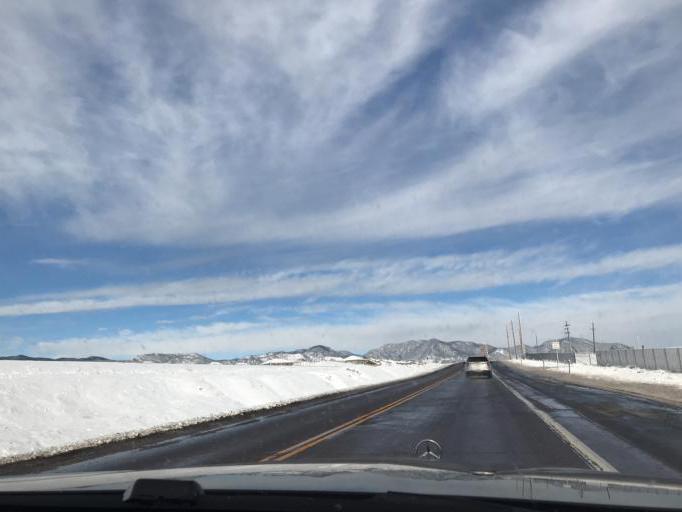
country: US
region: Colorado
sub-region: Jefferson County
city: Applewood
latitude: 39.8528
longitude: -105.1816
